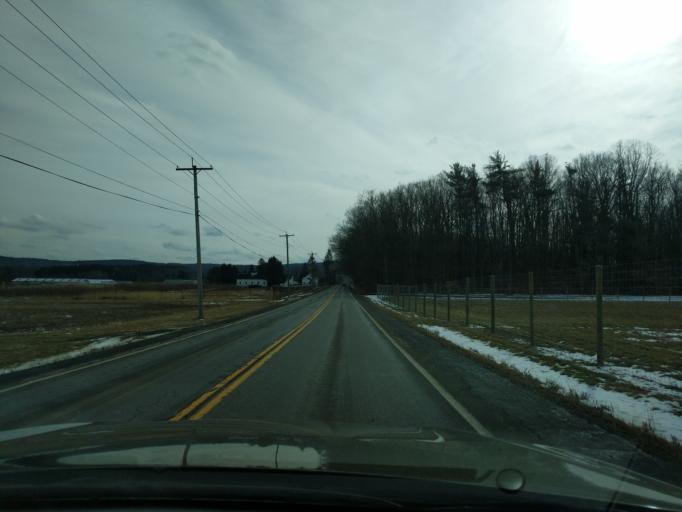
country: US
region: New York
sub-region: Tompkins County
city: Northeast Ithaca
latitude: 42.4488
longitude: -76.4494
